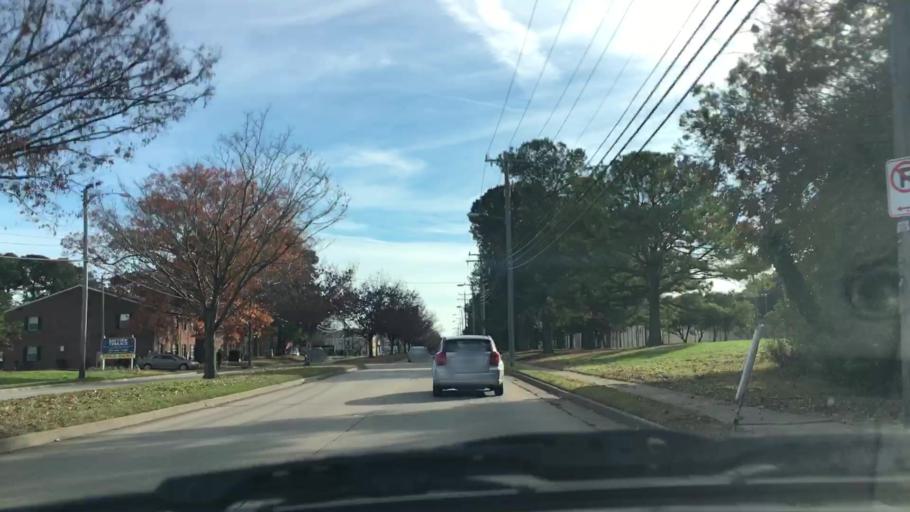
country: US
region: Virginia
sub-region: City of Norfolk
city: Norfolk
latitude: 36.9300
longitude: -76.2534
